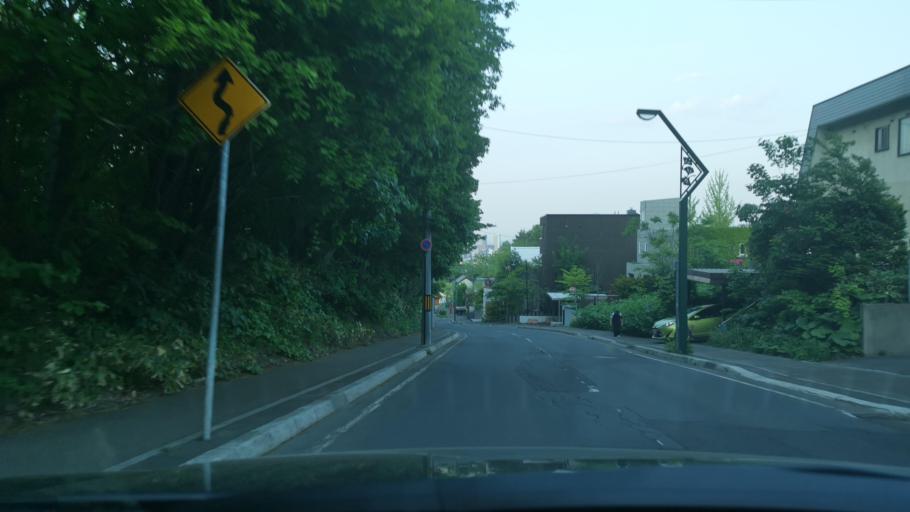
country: JP
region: Hokkaido
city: Sapporo
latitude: 43.0373
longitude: 141.3144
